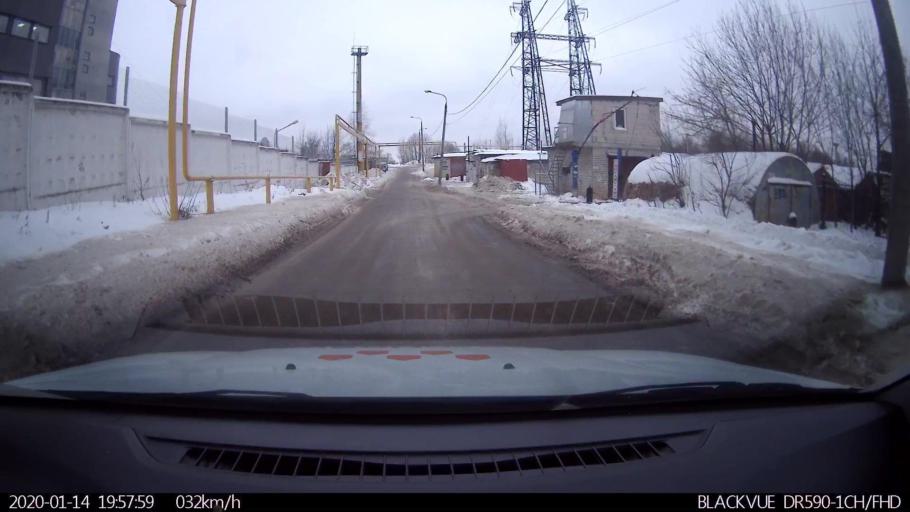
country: RU
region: Nizjnij Novgorod
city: Nizhniy Novgorod
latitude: 56.2356
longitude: 43.9407
